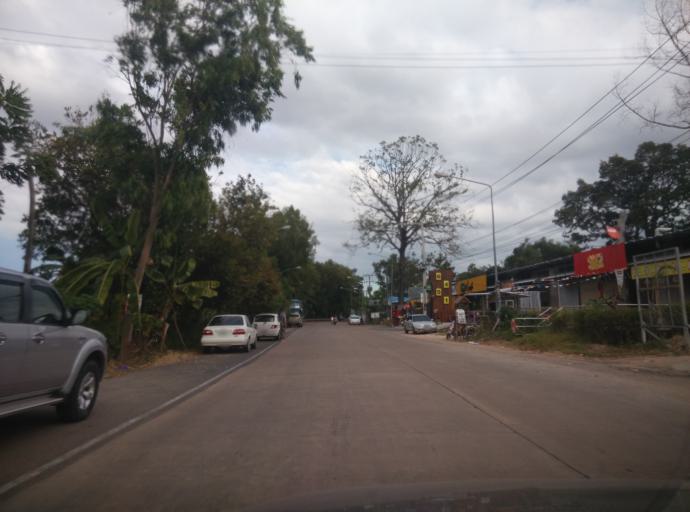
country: TH
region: Sisaket
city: Si Sa Ket
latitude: 15.1229
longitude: 104.3437
